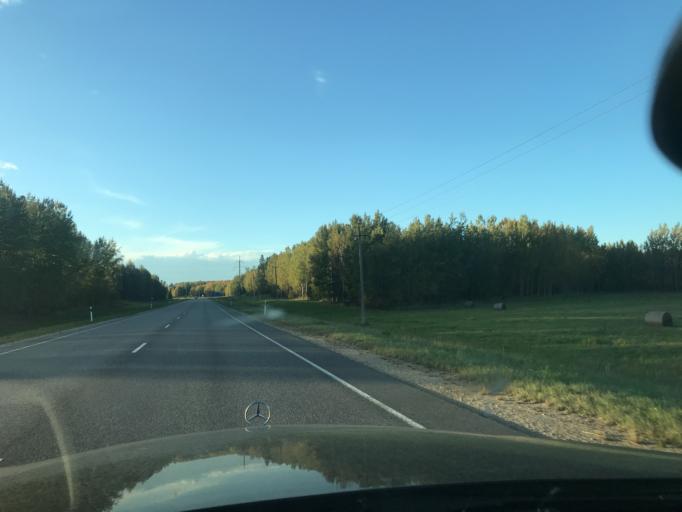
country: EE
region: Vorumaa
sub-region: Voru linn
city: Voru
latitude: 57.8444
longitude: 27.0470
